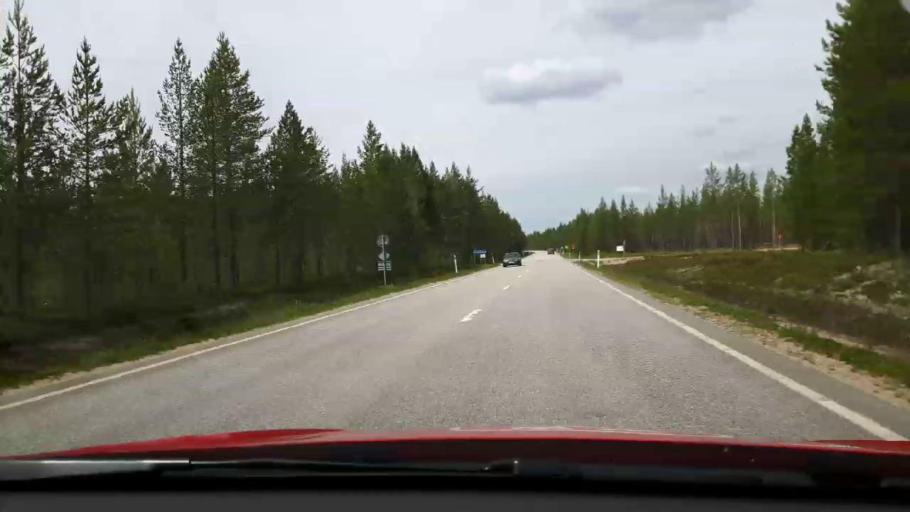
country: SE
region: Jaemtland
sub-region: Harjedalens Kommun
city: Sveg
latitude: 62.0555
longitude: 14.3018
